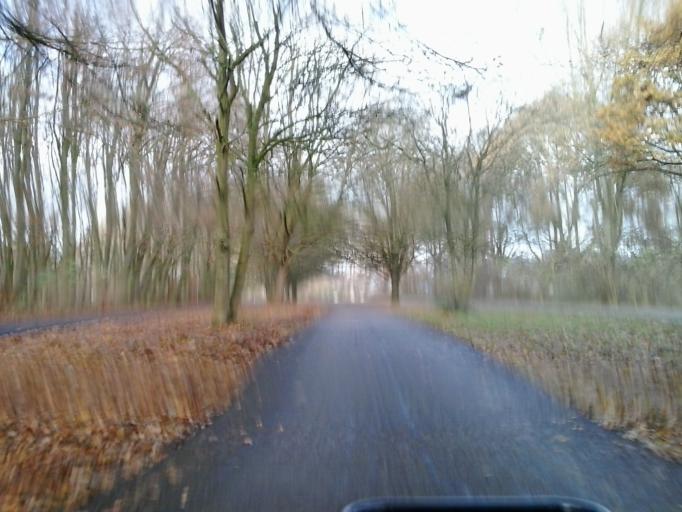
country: NL
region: South Holland
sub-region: Gemeente Lansingerland
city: Bergschenhoek
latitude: 51.9714
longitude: 4.5204
